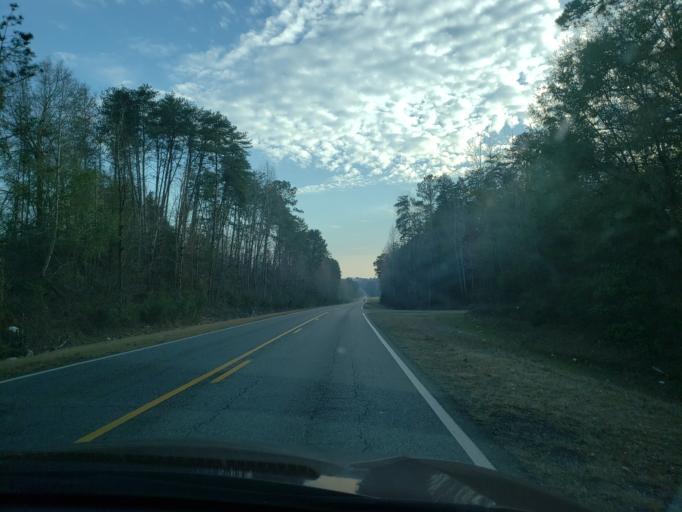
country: US
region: Alabama
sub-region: Hale County
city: Greensboro
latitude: 32.7295
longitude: -87.5880
